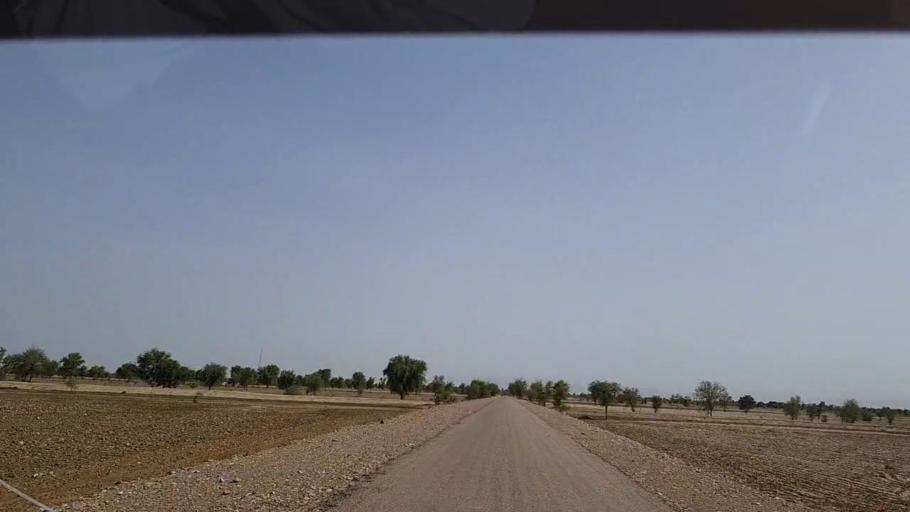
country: PK
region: Sindh
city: Johi
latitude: 26.6488
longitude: 67.5044
